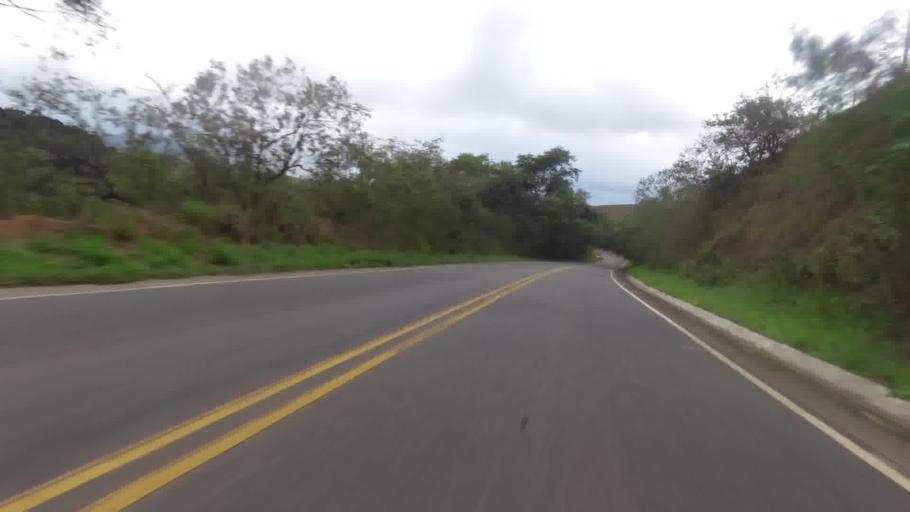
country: BR
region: Espirito Santo
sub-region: Alfredo Chaves
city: Alfredo Chaves
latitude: -20.6639
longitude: -40.7171
